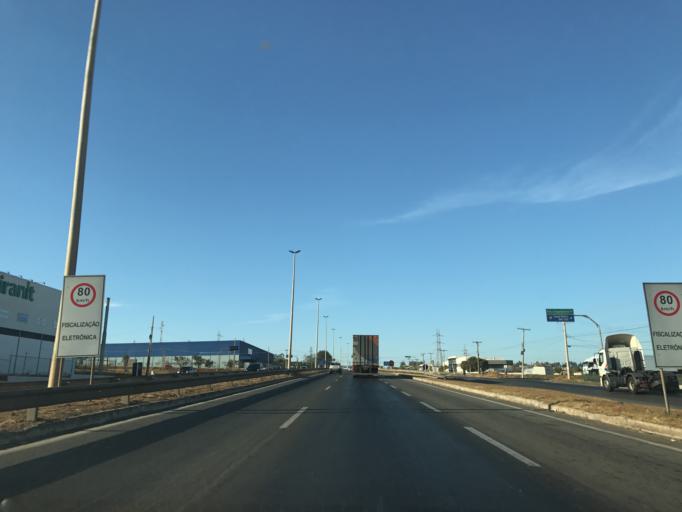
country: BR
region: Goias
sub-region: Aparecida De Goiania
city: Aparecida de Goiania
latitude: -16.7856
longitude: -49.2376
